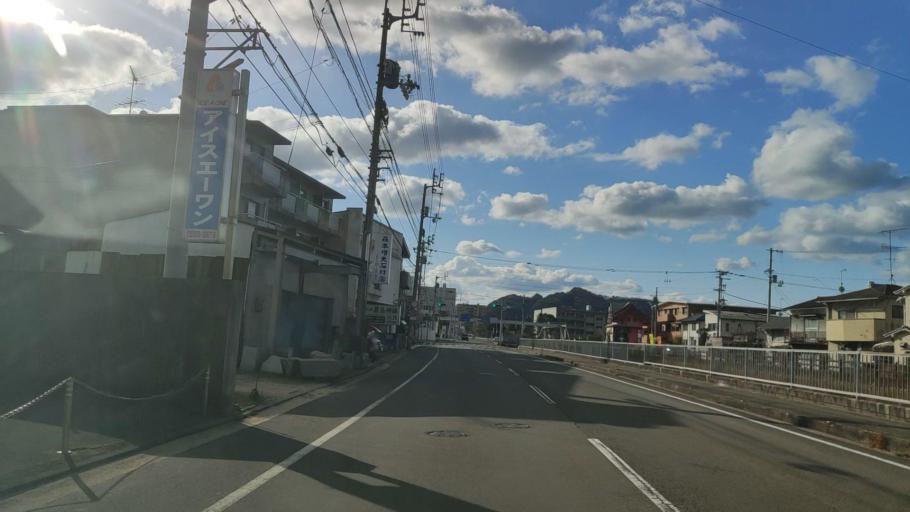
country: JP
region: Ehime
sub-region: Shikoku-chuo Shi
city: Matsuyama
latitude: 33.8595
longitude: 132.7194
